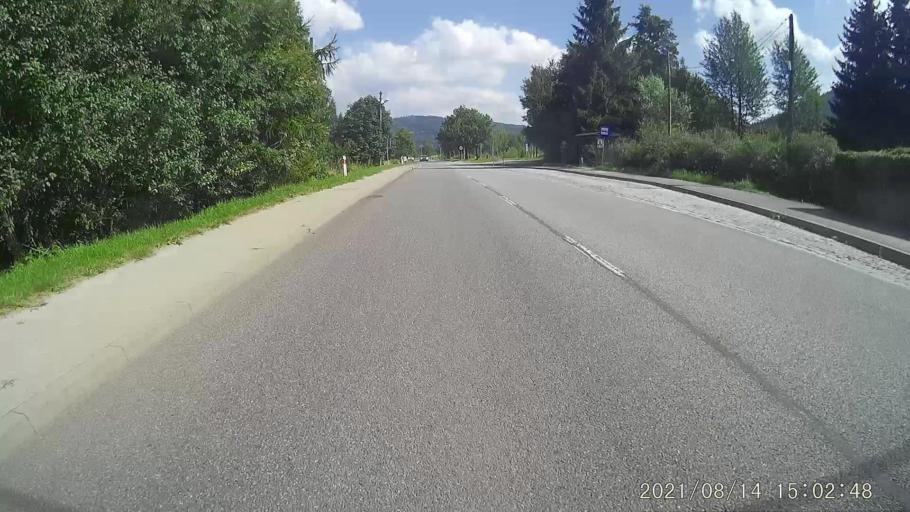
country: PL
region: Lower Silesian Voivodeship
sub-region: Powiat walbrzyski
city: Jedlina-Zdroj
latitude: 50.7223
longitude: 16.3348
